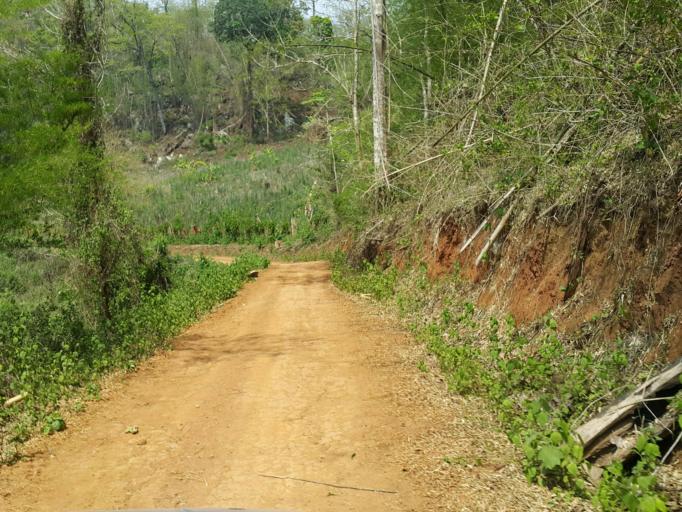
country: TH
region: Chiang Mai
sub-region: Amphoe Chiang Dao
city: Chiang Dao
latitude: 19.3133
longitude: 98.7249
